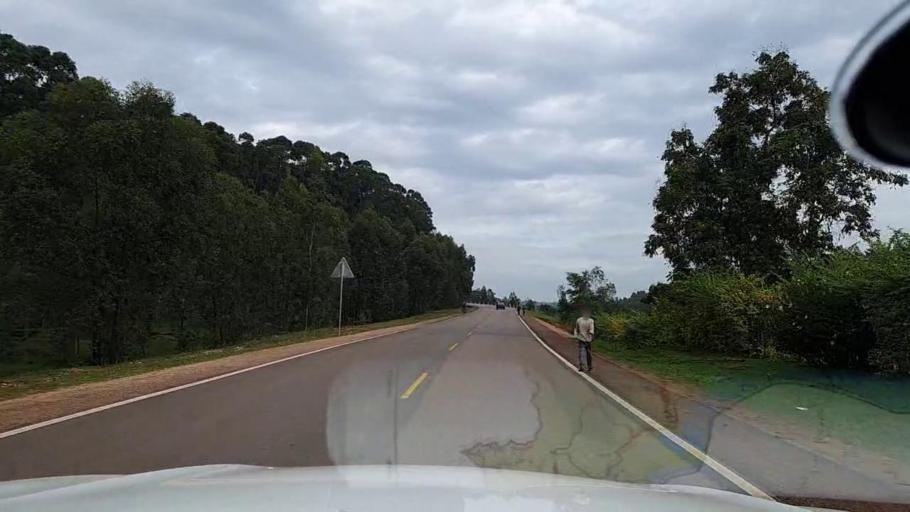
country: RW
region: Southern Province
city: Butare
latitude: -2.5643
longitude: 29.7236
